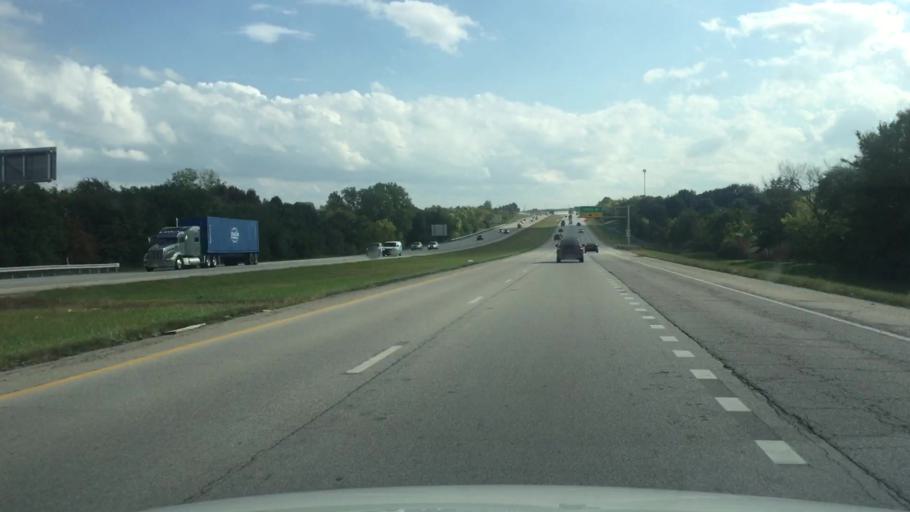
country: US
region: Kansas
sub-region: Johnson County
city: Lenexa
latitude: 38.8519
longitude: -94.6773
